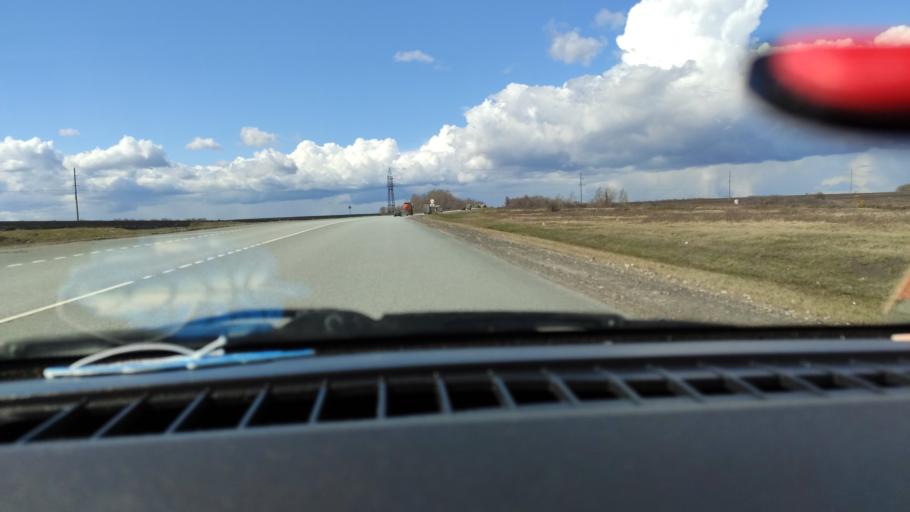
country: RU
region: Samara
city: Obsharovka
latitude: 53.2128
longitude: 48.7740
